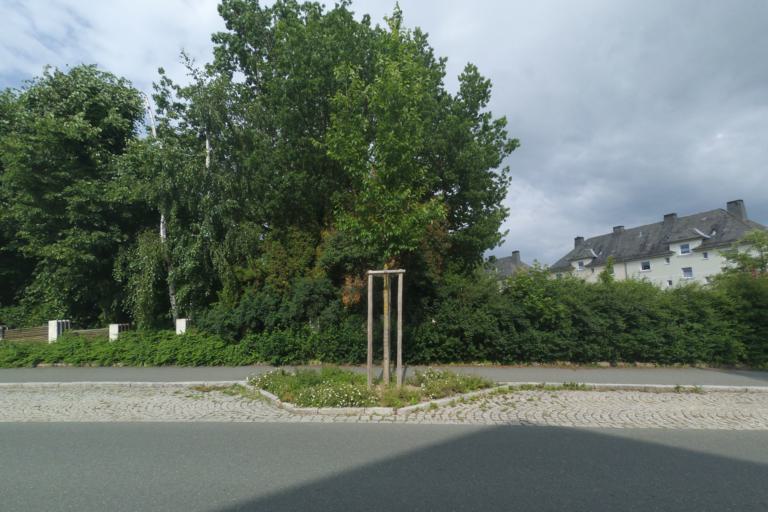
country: DE
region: Bavaria
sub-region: Upper Franconia
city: Munchberg
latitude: 50.1862
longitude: 11.7903
